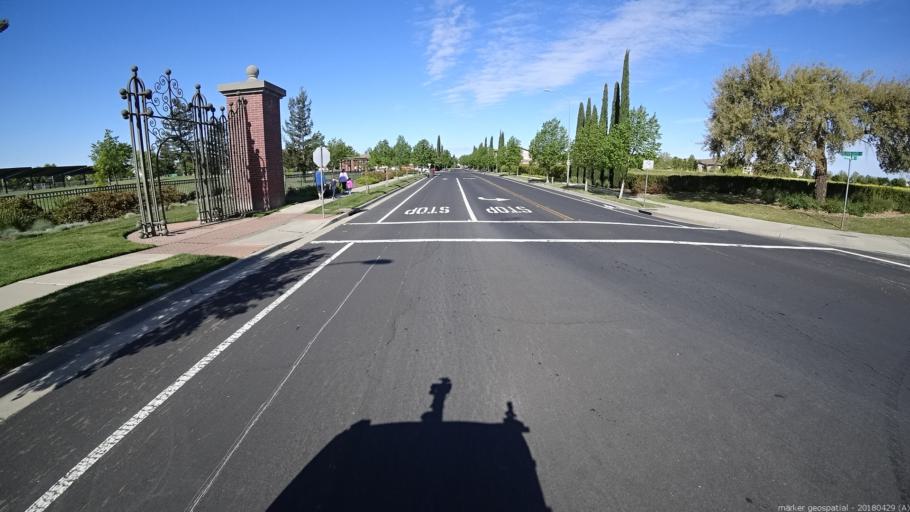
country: US
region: California
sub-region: Yolo County
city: West Sacramento
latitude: 38.5423
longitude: -121.5675
